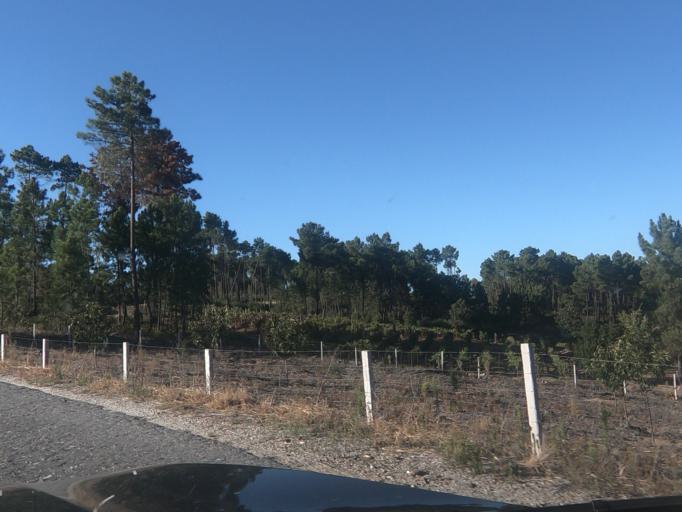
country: PT
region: Vila Real
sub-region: Sabrosa
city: Sabrosa
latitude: 41.3222
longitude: -7.5858
